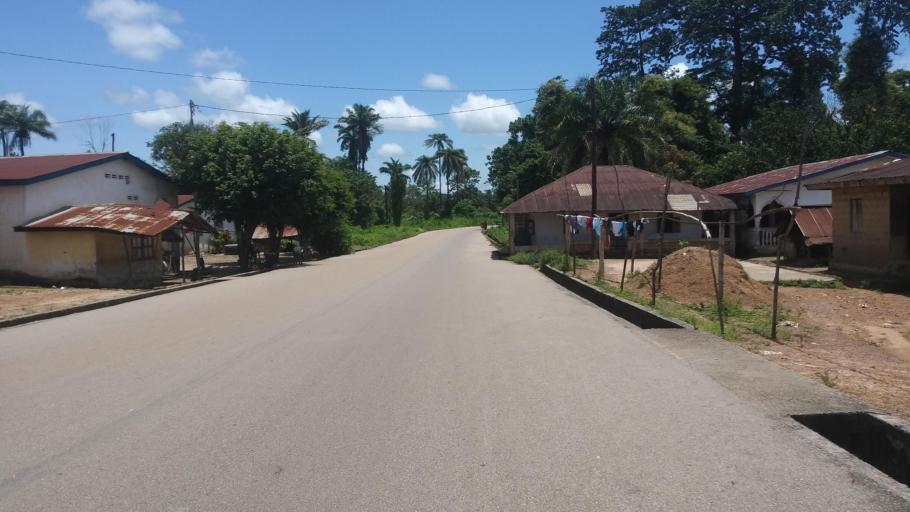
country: SL
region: Northern Province
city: Makeni
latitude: 8.8794
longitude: -12.0232
